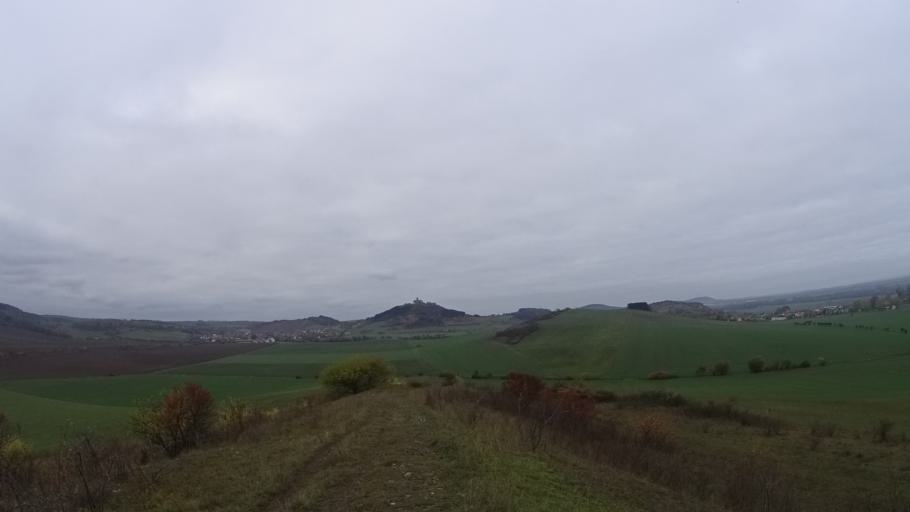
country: DE
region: Thuringia
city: Arnstadt
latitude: 50.8535
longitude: 10.9115
